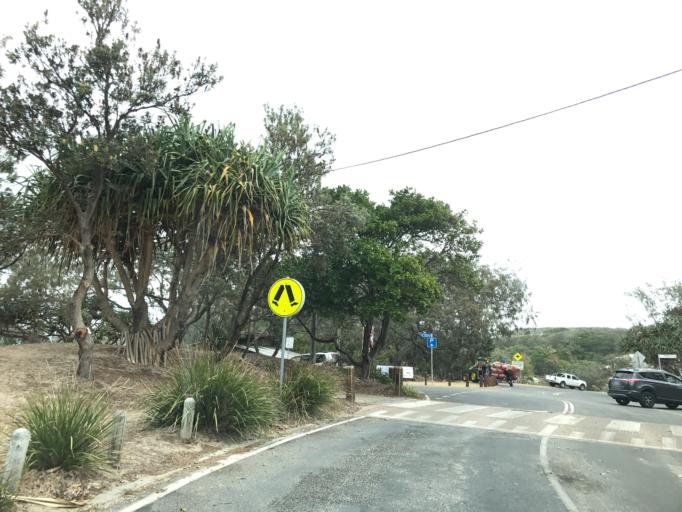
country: AU
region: Queensland
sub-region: Redland
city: Victoria Point
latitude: -27.4340
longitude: 153.5436
